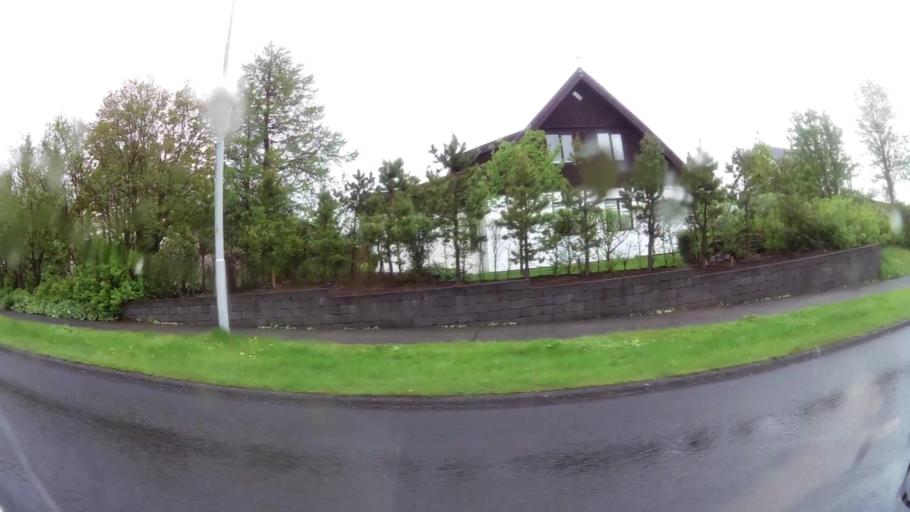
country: IS
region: Capital Region
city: Reykjavik
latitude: 64.0959
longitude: -21.8454
